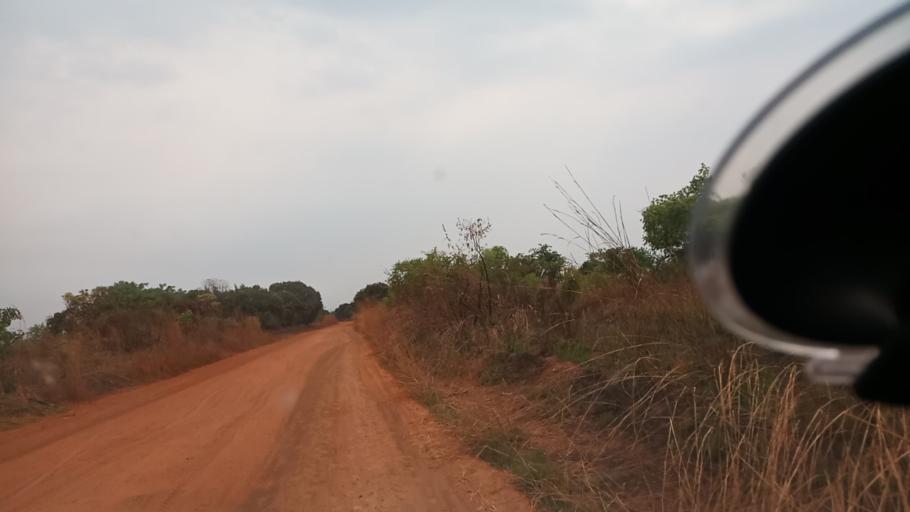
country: ZM
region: Luapula
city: Nchelenge
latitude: -9.1435
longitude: 28.2923
